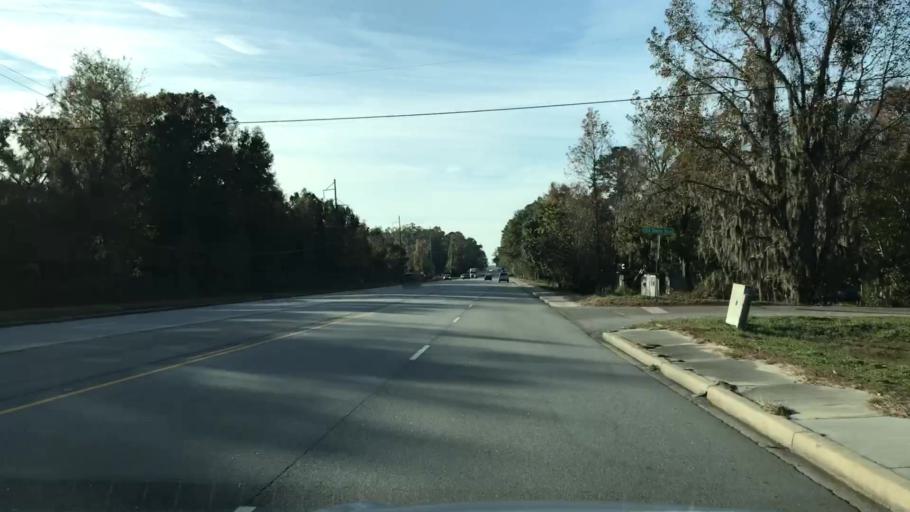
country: US
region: South Carolina
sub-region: Beaufort County
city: Laurel Bay
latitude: 32.5610
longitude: -80.7438
